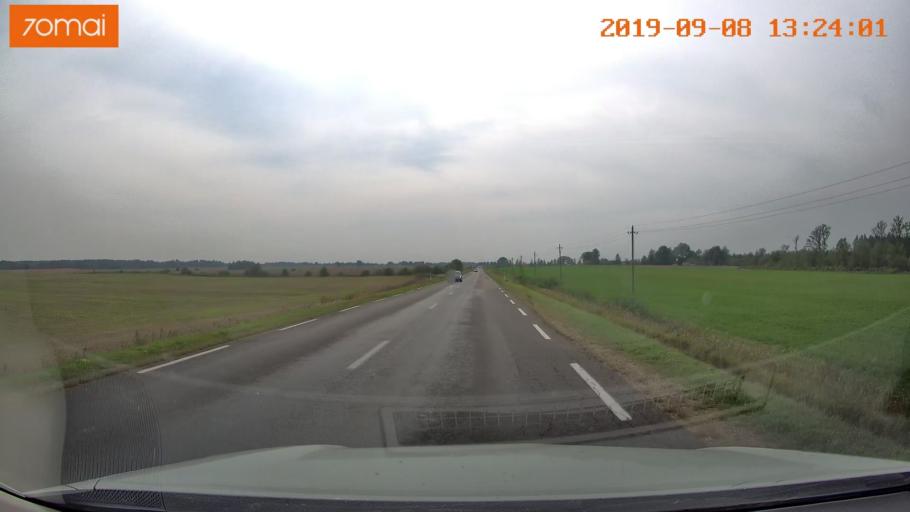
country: LT
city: Jieznas
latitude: 54.6309
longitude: 24.1757
